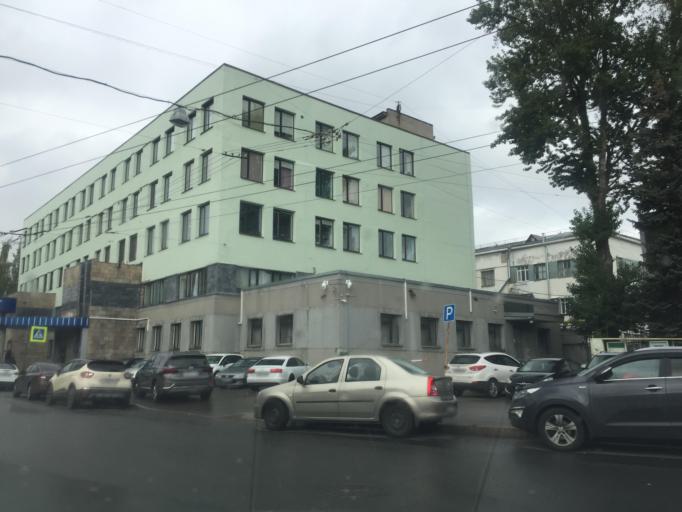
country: RU
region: St.-Petersburg
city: Sosnovka
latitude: 60.0086
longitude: 30.3612
